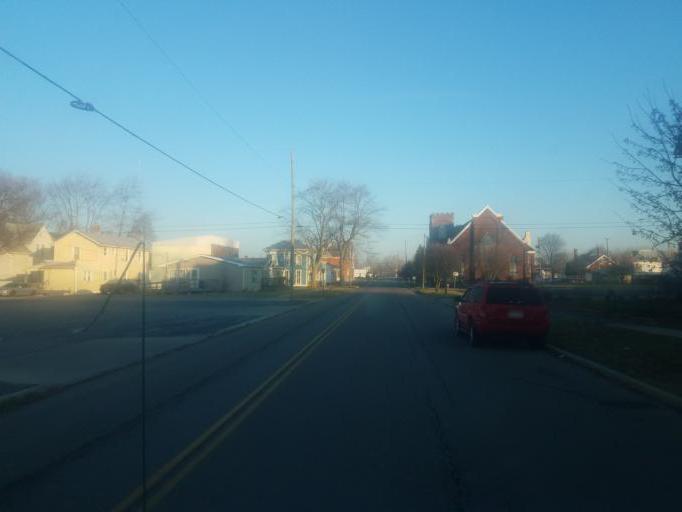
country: US
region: Ohio
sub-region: Crawford County
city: Bucyrus
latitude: 40.8070
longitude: -82.9723
